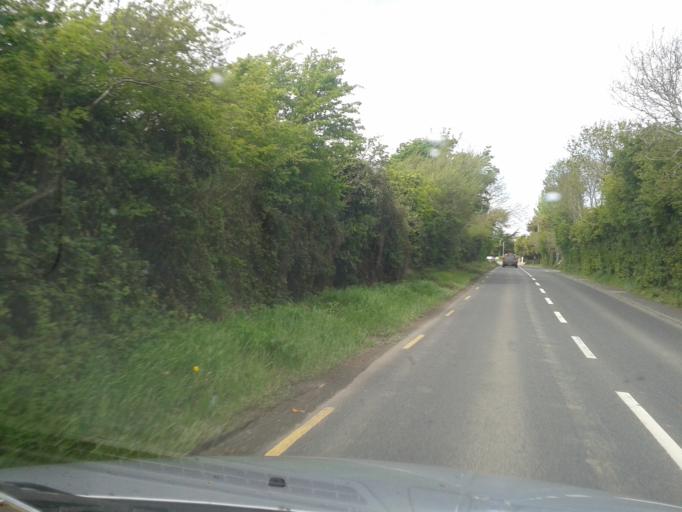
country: IE
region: Leinster
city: Kinsealy-Drinan
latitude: 53.4516
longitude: -6.1901
